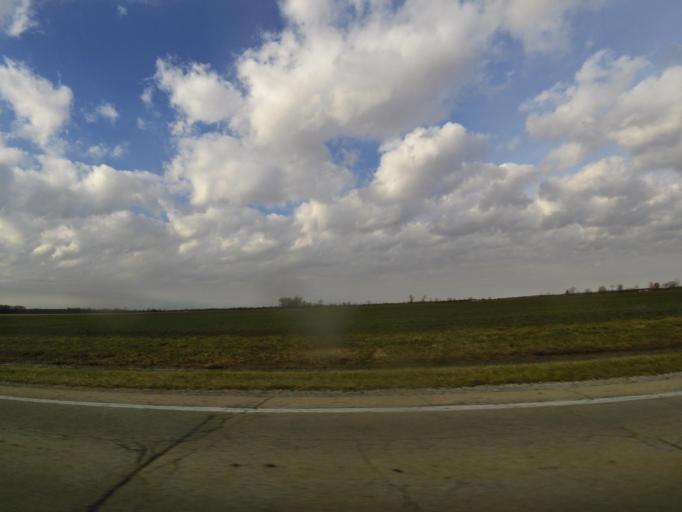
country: US
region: Illinois
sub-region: Fayette County
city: Ramsey
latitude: 39.2108
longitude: -89.1008
